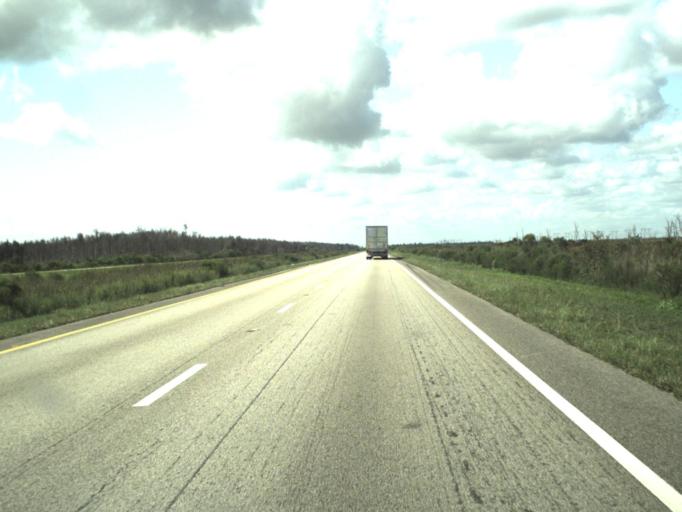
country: US
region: Florida
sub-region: Miami-Dade County
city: Palm Springs North
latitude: 25.9900
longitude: -80.4324
